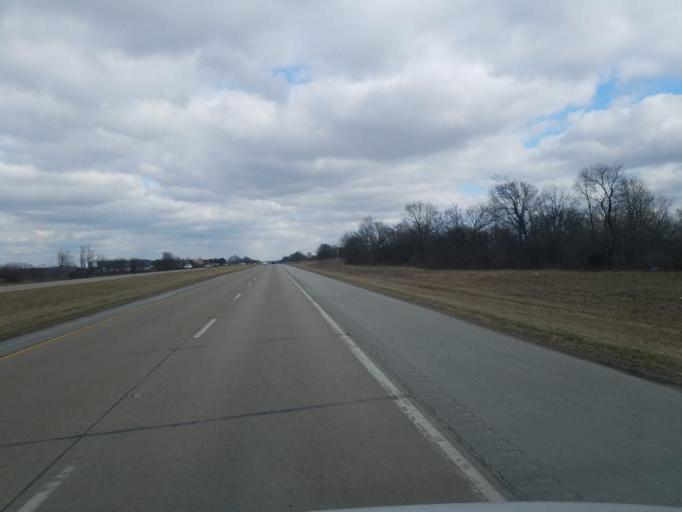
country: US
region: Indiana
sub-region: Hendricks County
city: Danville
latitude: 39.7568
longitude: -86.4809
